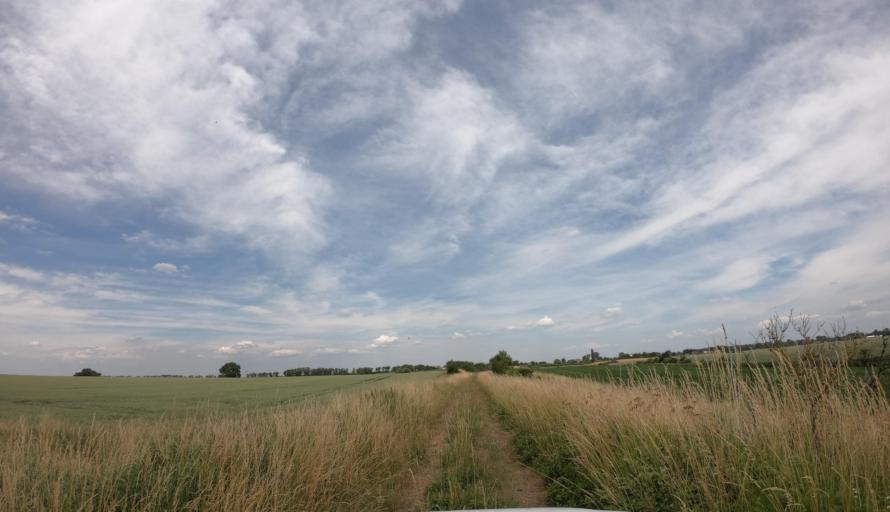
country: PL
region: West Pomeranian Voivodeship
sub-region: Powiat pyrzycki
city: Kozielice
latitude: 53.1309
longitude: 14.8510
